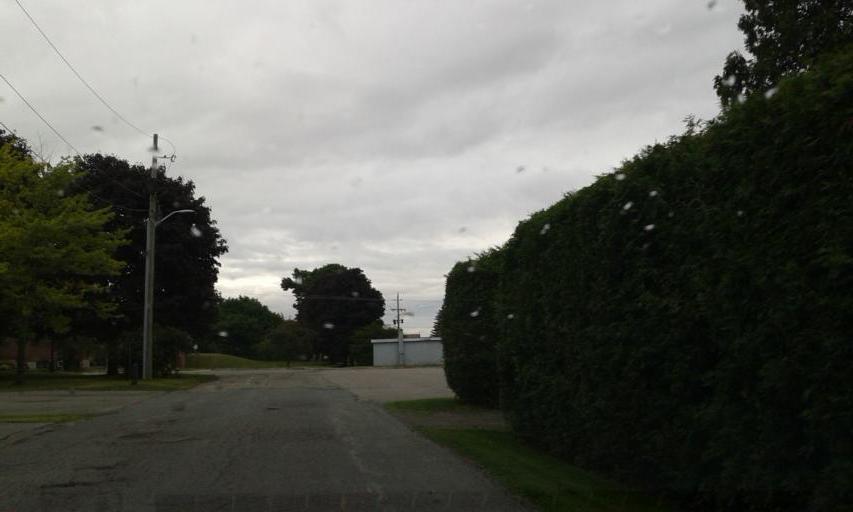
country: CA
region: Ontario
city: Prescott
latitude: 44.7044
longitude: -75.5219
